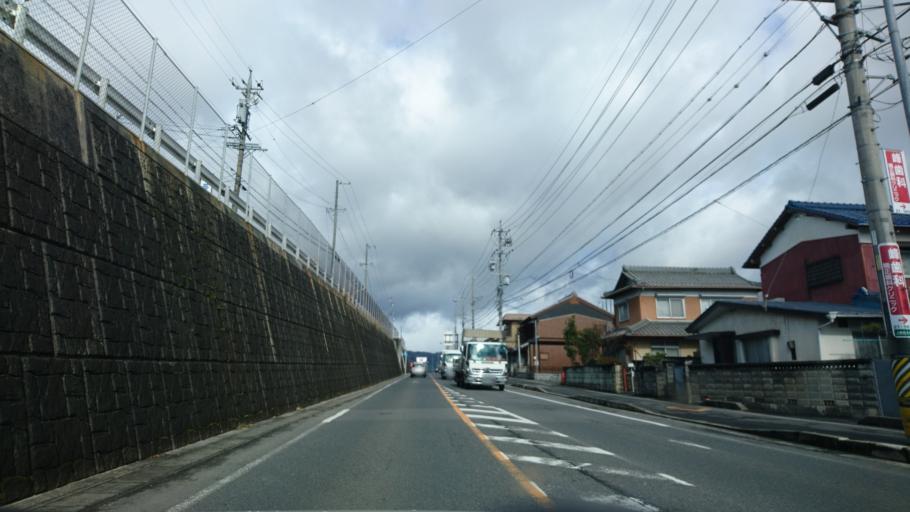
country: JP
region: Mie
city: Ueno-ebisumachi
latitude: 34.7680
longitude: 136.1233
